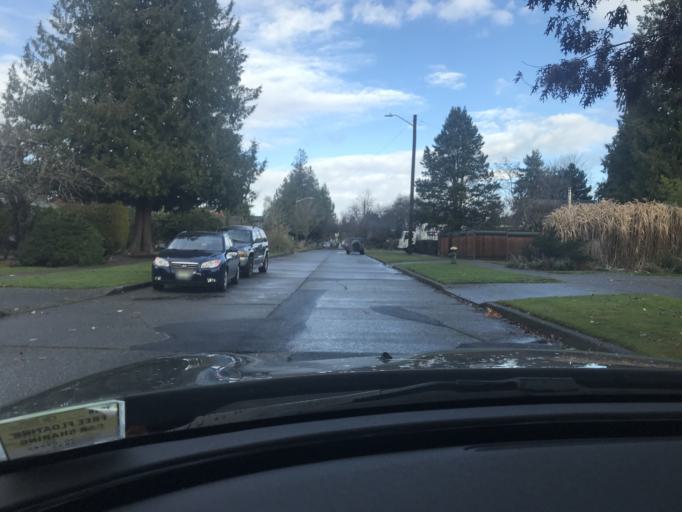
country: US
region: Washington
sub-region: King County
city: White Center
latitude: 47.5217
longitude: -122.3713
